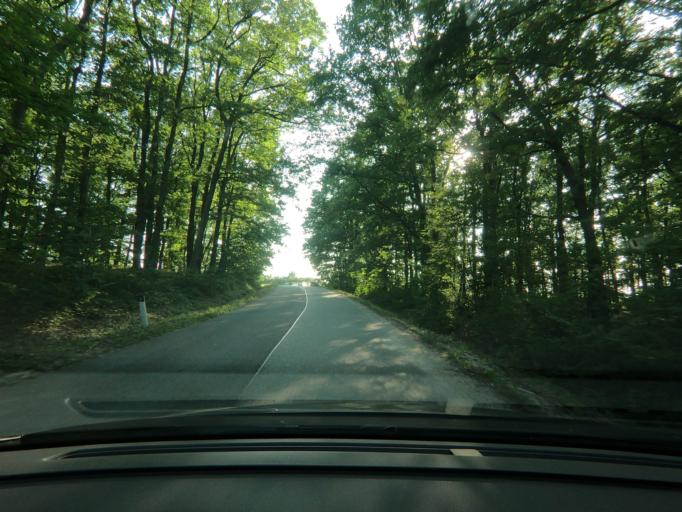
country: SK
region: Nitriansky
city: Stara Tura
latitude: 48.7288
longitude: 17.6715
